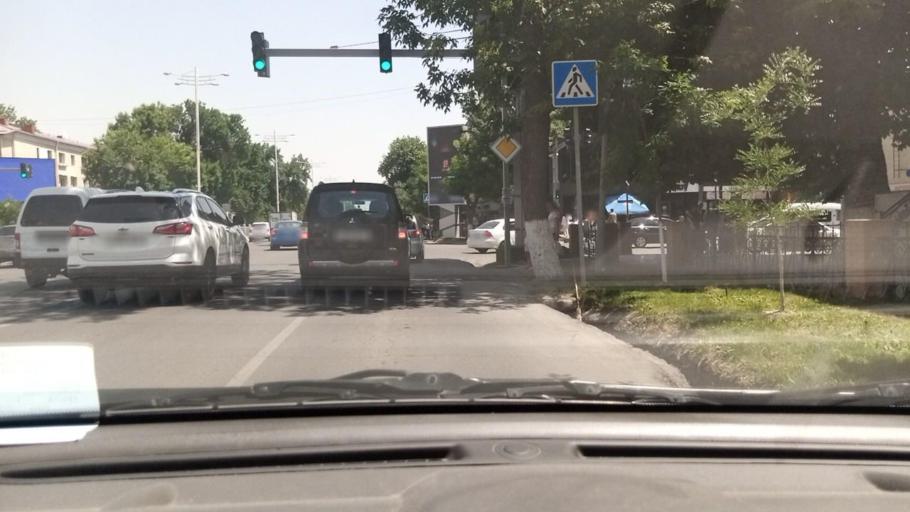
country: UZ
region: Toshkent Shahri
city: Tashkent
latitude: 41.2884
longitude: 69.2289
